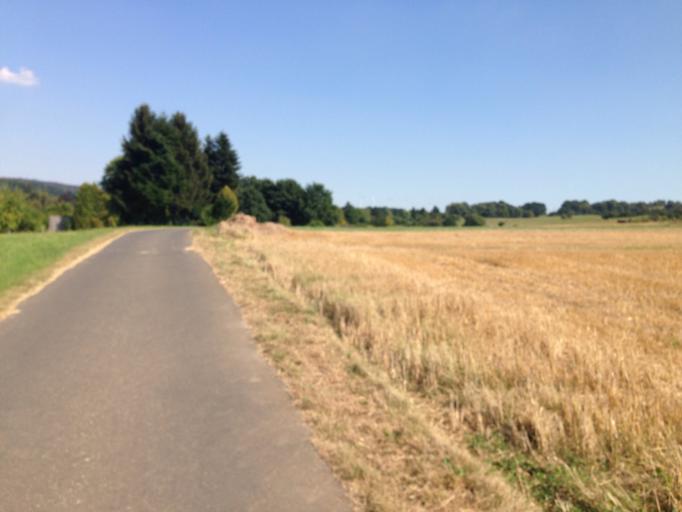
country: DE
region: Hesse
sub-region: Regierungsbezirk Giessen
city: Rabenau
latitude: 50.6739
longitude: 8.8538
